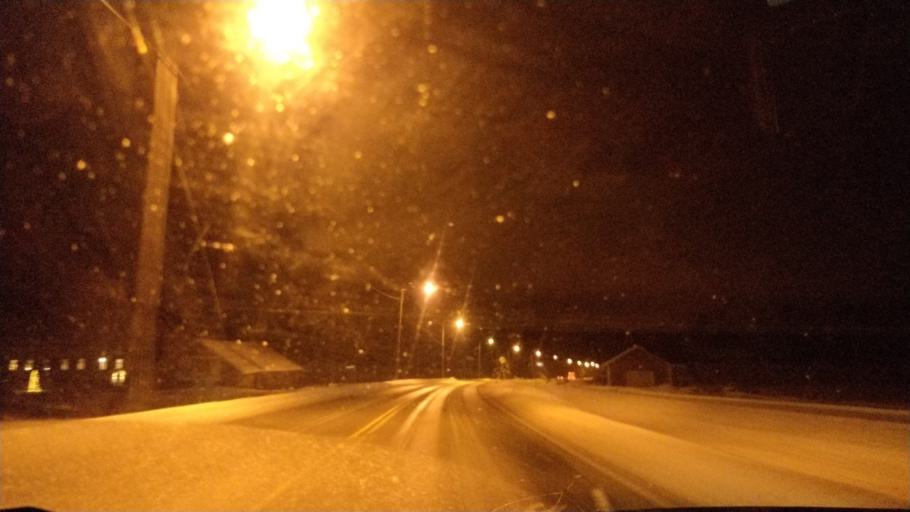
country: FI
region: Lapland
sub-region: Rovaniemi
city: Rovaniemi
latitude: 66.3173
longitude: 25.3612
